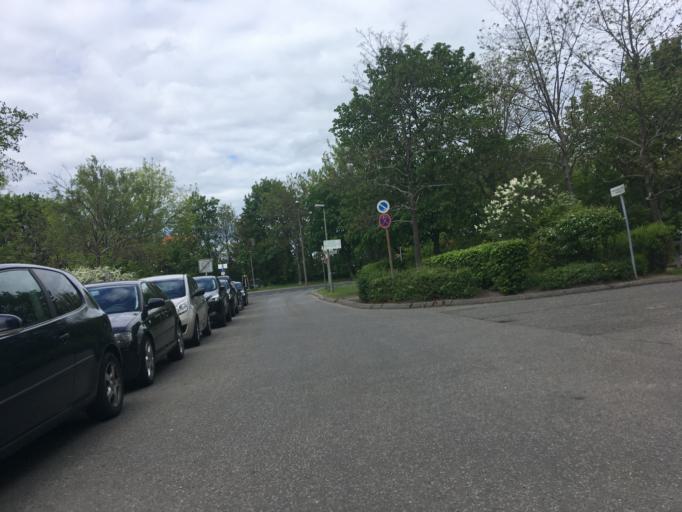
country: DE
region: Berlin
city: Biesdorf
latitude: 52.5335
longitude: 13.5468
